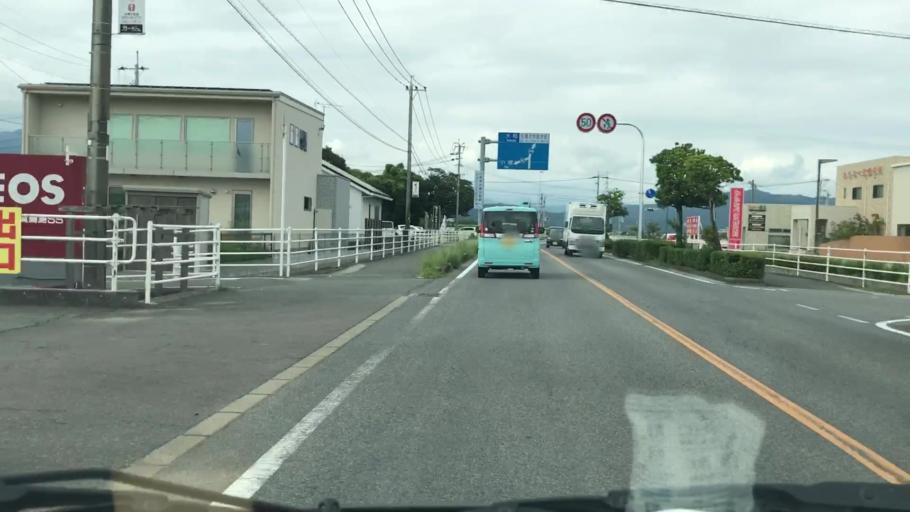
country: JP
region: Saga Prefecture
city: Saga-shi
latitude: 33.2746
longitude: 130.2607
